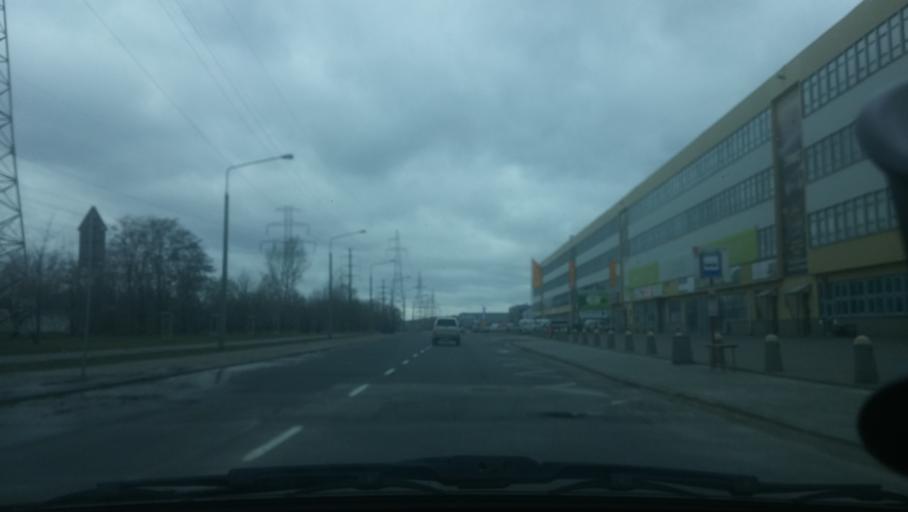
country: PL
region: Masovian Voivodeship
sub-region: Warszawa
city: Ursus
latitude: 52.2026
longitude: 20.8736
